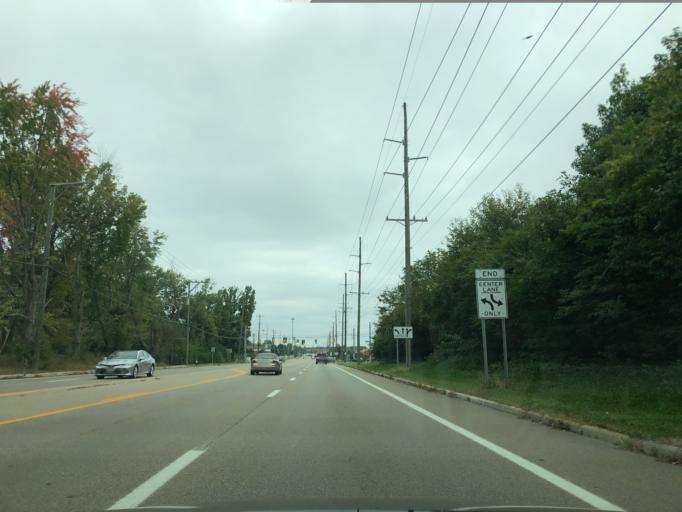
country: US
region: Ohio
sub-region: Hamilton County
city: Sixteen Mile Stand
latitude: 39.2848
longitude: -84.3122
